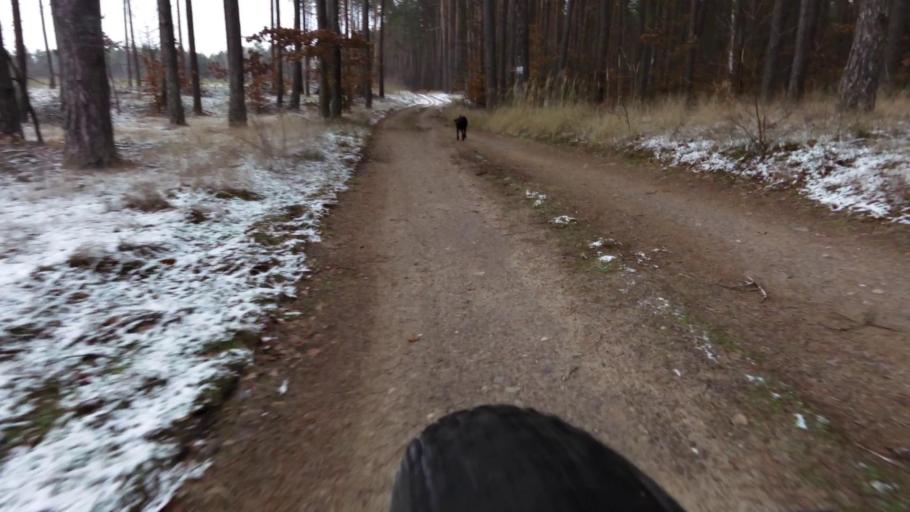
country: PL
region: West Pomeranian Voivodeship
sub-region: Powiat walecki
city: Miroslawiec
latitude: 53.2971
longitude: 16.0635
